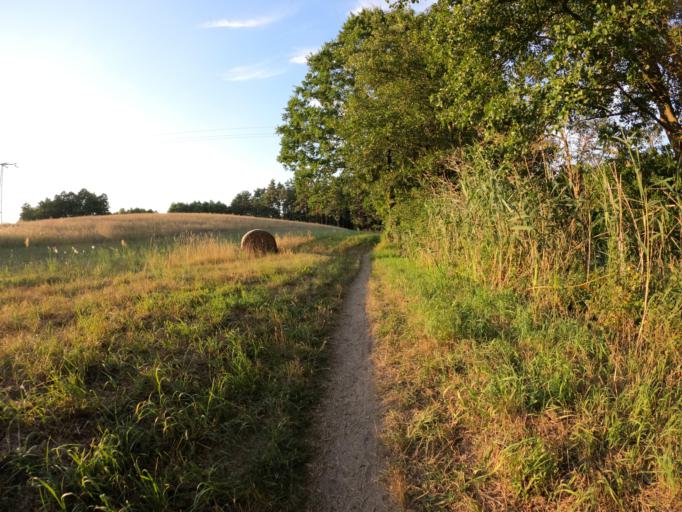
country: DE
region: Brandenburg
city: Templin
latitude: 53.1386
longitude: 13.5410
